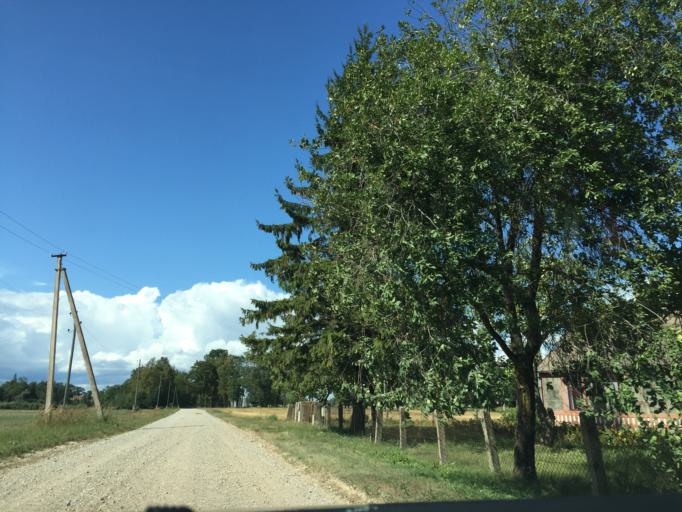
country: LT
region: Siauliu apskritis
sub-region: Joniskis
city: Joniskis
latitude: 56.3384
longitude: 23.5572
